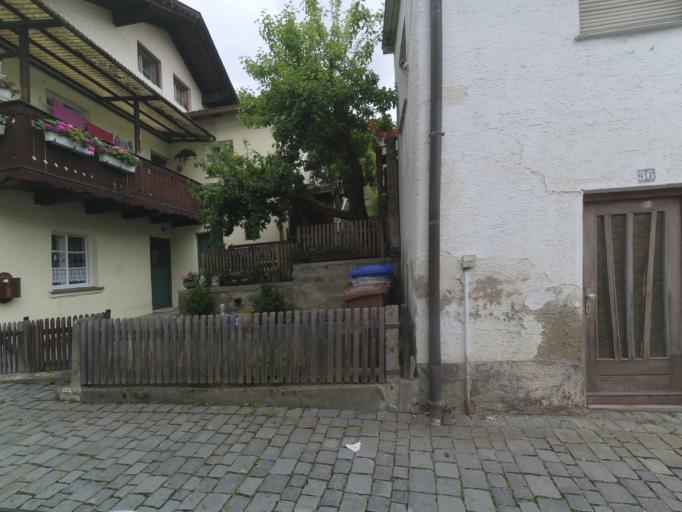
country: DE
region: Bavaria
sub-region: Lower Bavaria
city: Regen
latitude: 48.9713
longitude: 13.1245
